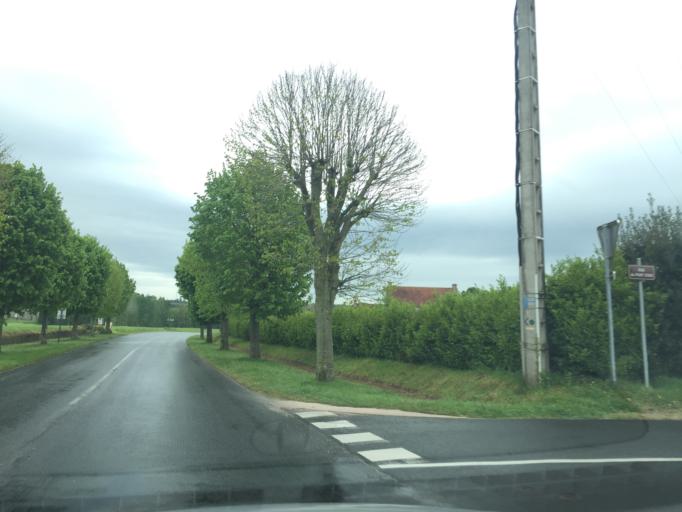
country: FR
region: Brittany
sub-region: Departement des Cotes-d'Armor
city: Crehen
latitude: 48.5443
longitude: -2.2294
